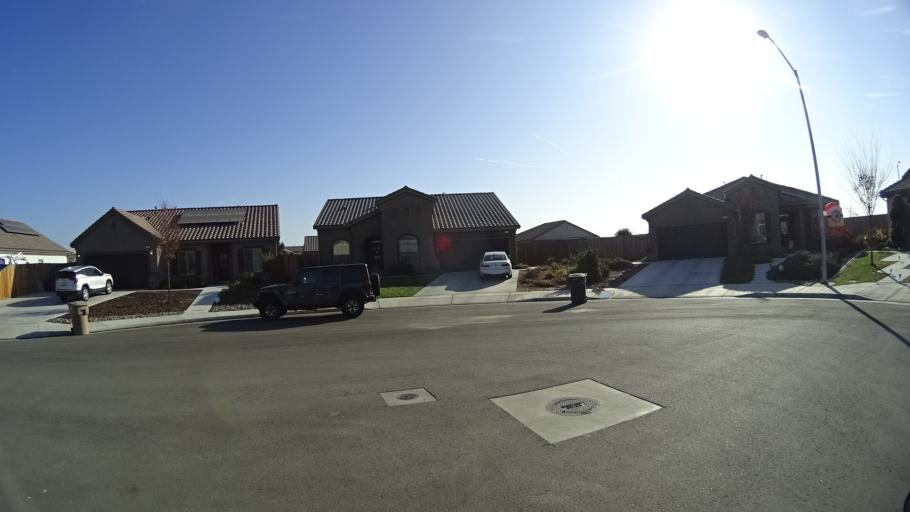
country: US
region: California
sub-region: Kern County
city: Greenfield
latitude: 35.2677
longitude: -119.0708
